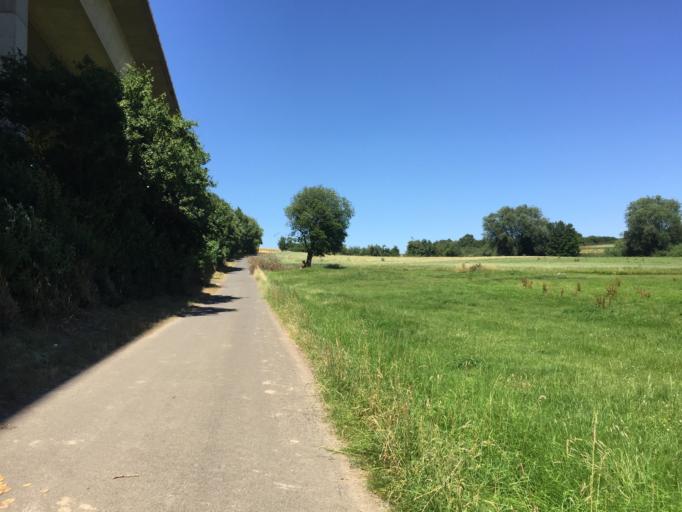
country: DE
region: Hesse
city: Beuern
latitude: 50.6178
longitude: 8.8101
